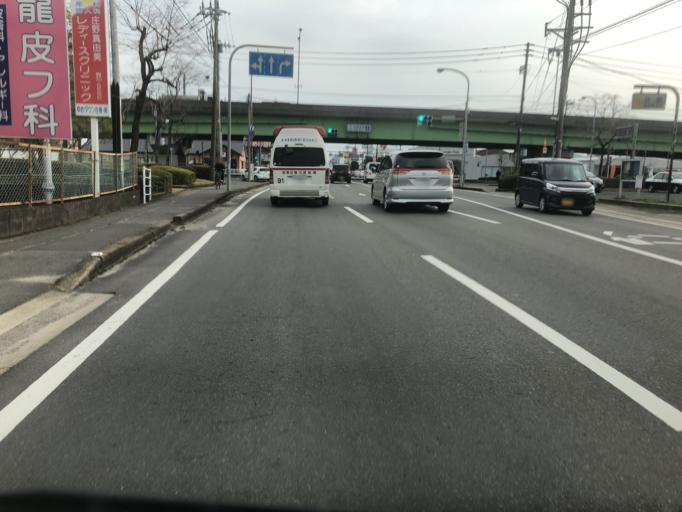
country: JP
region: Saga Prefecture
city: Saga-shi
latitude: 33.2727
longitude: 130.2710
